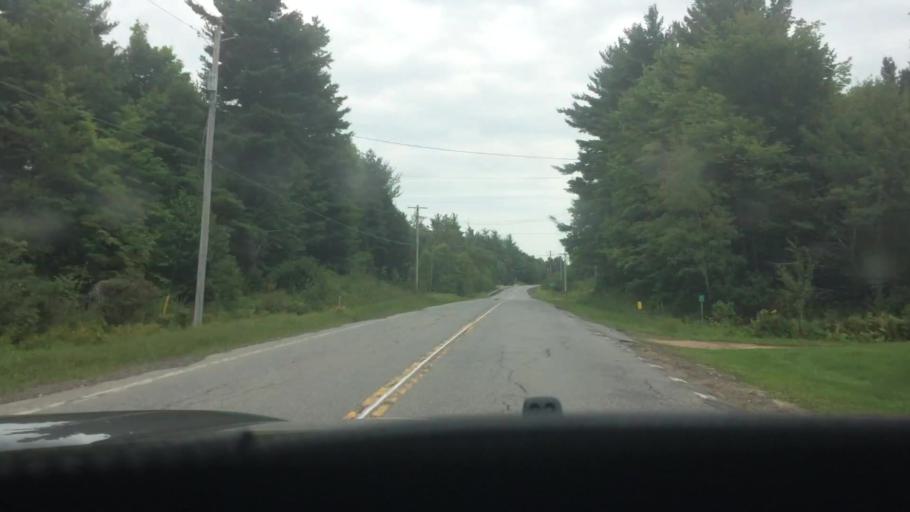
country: US
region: New York
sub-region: St. Lawrence County
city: Hannawa Falls
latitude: 44.5473
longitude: -74.9483
